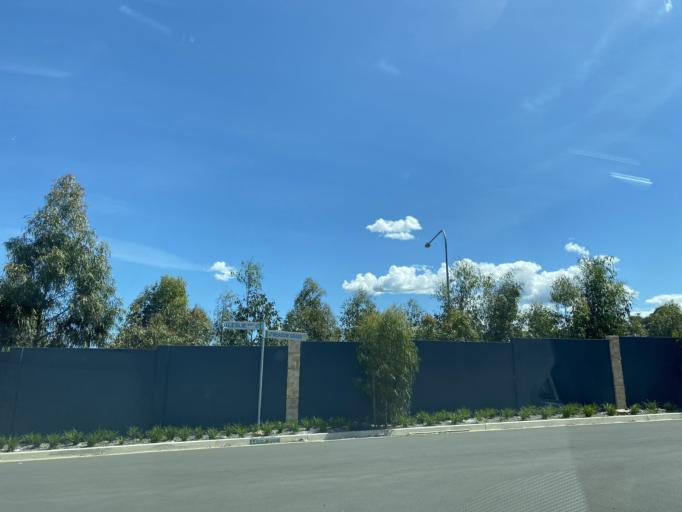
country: AU
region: New South Wales
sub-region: Campbelltown Municipality
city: Denham Court
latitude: -33.9905
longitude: 150.7910
